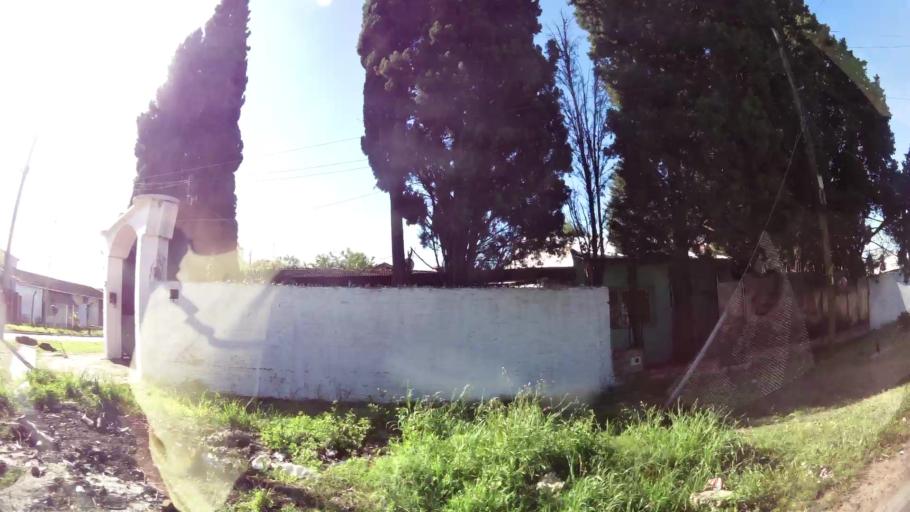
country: AR
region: Buenos Aires
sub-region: Partido de Almirante Brown
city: Adrogue
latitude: -34.8282
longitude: -58.3510
